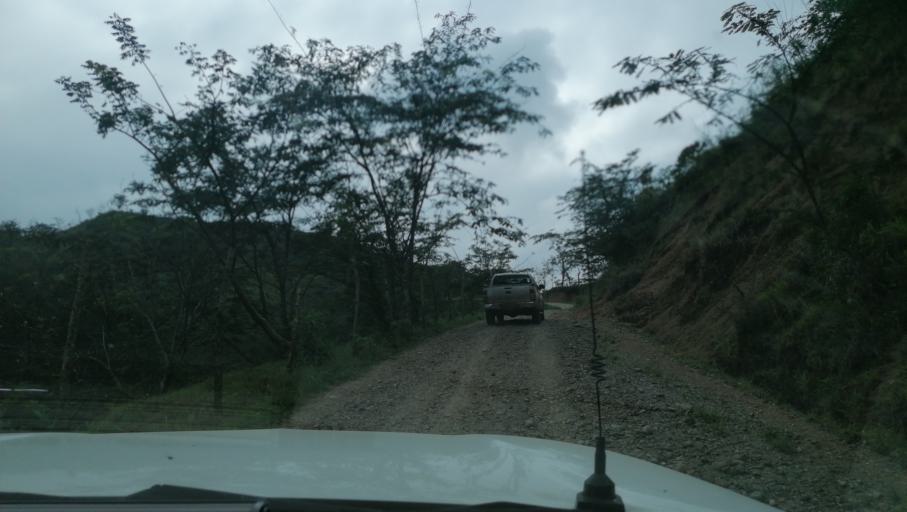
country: MX
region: Chiapas
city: Ostuacan
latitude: 17.3458
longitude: -93.3085
